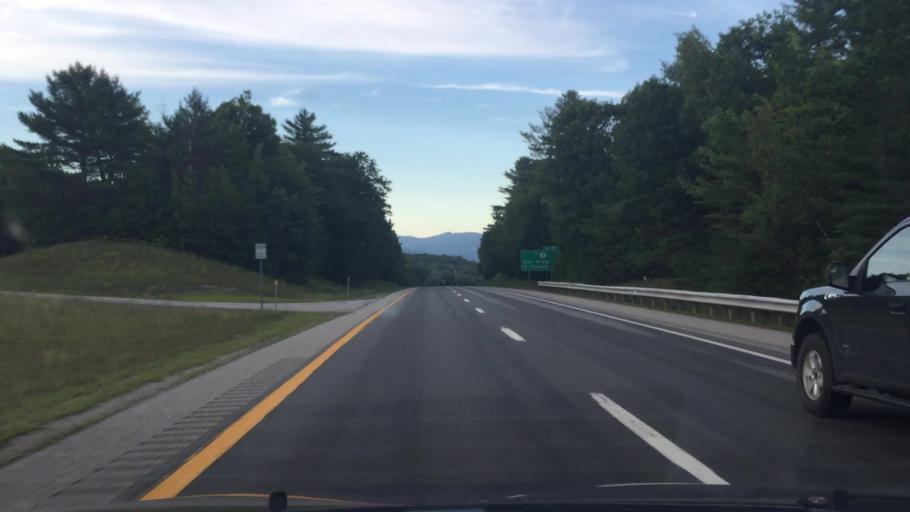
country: US
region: New Hampshire
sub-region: Grafton County
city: Plymouth
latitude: 43.8047
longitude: -71.6750
